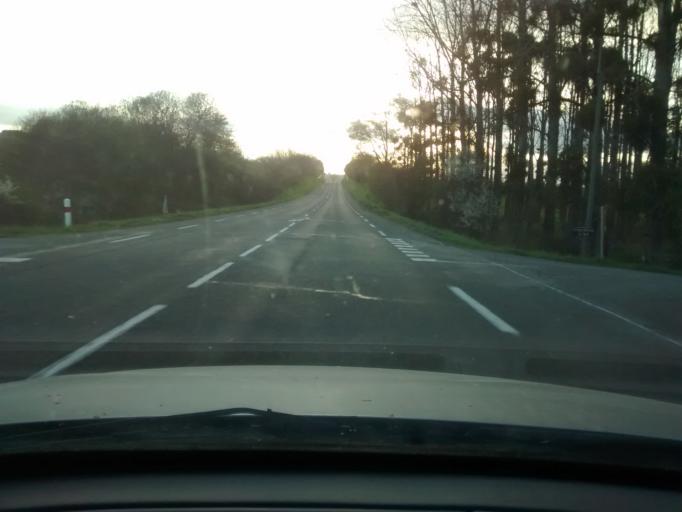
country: FR
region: Pays de la Loire
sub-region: Departement de la Mayenne
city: Vaiges
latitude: 48.0377
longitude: -0.4185
